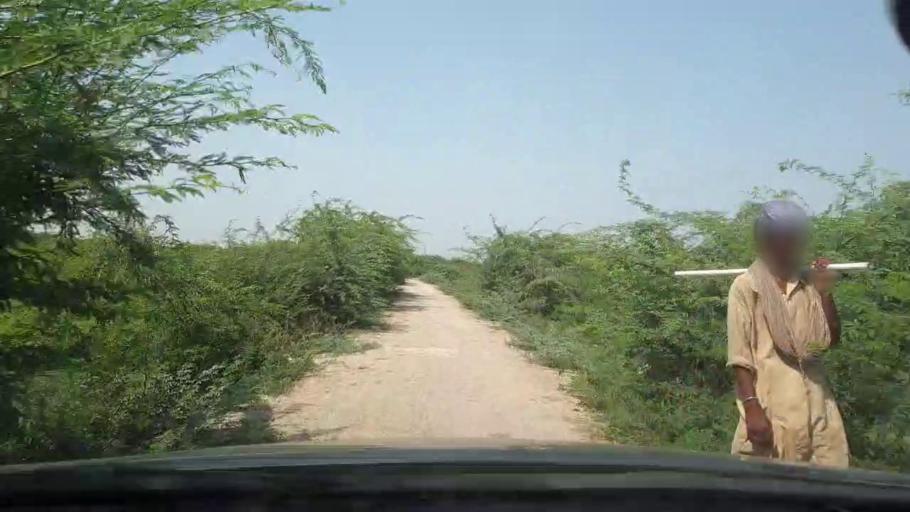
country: PK
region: Sindh
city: Naukot
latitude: 24.8121
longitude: 69.2720
